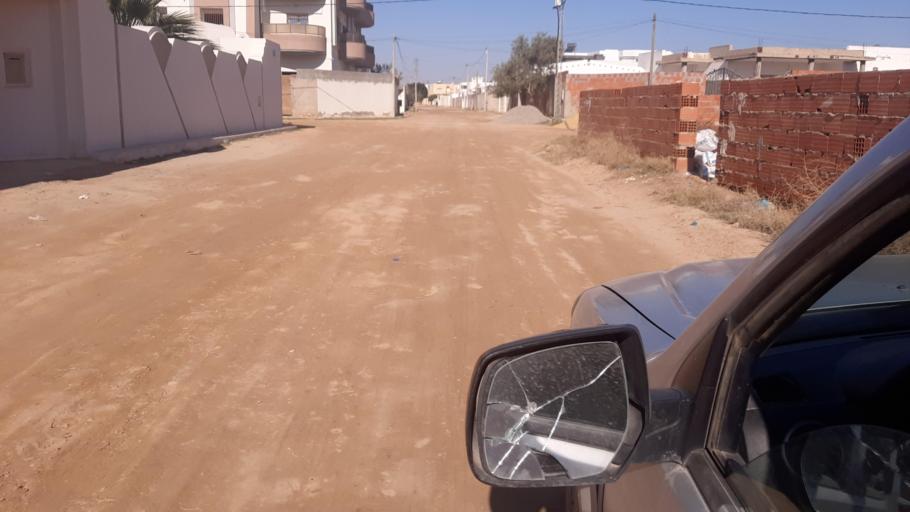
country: TN
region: Safaqis
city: Al Qarmadah
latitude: 34.7901
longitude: 10.8110
